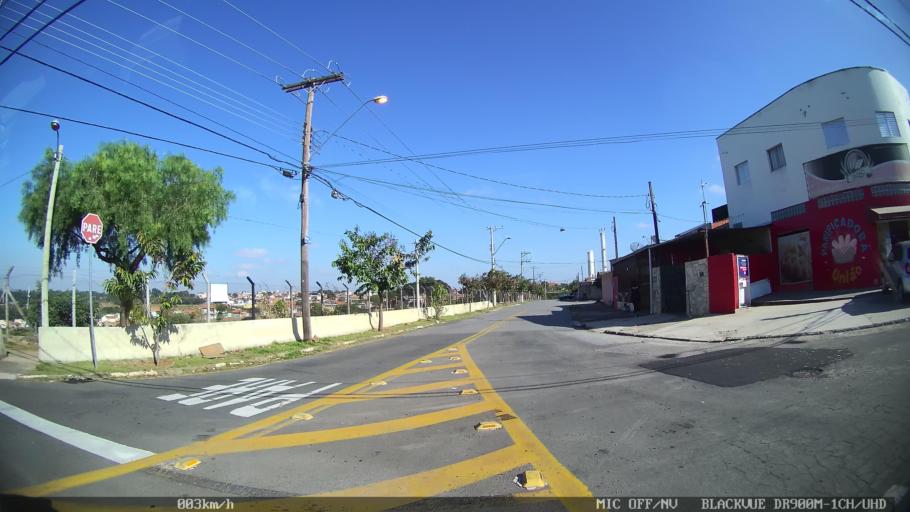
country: BR
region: Sao Paulo
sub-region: Campinas
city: Campinas
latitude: -22.9320
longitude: -47.1219
